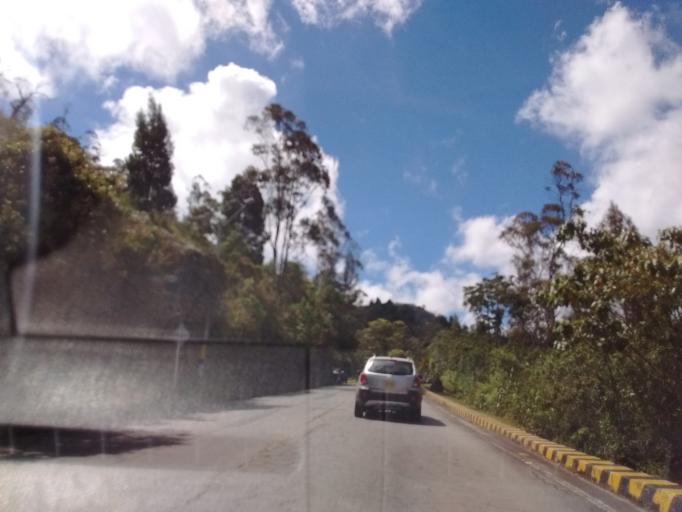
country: CO
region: Antioquia
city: Medellin
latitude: 6.2298
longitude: -75.5056
